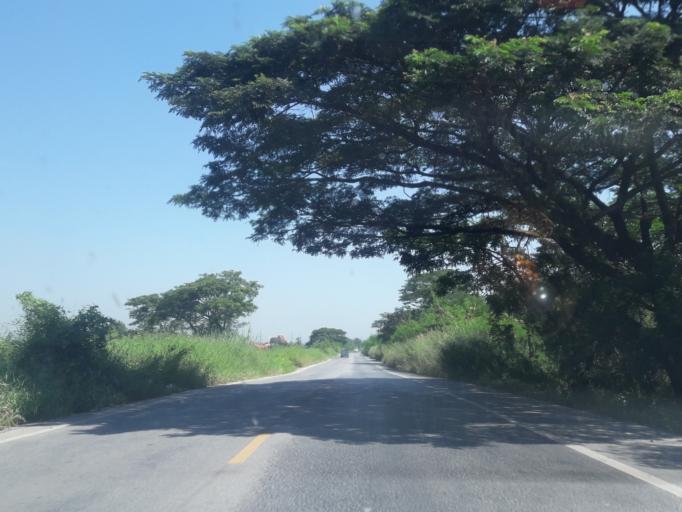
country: TH
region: Sara Buri
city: Nong Khae
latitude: 14.2963
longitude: 100.8381
